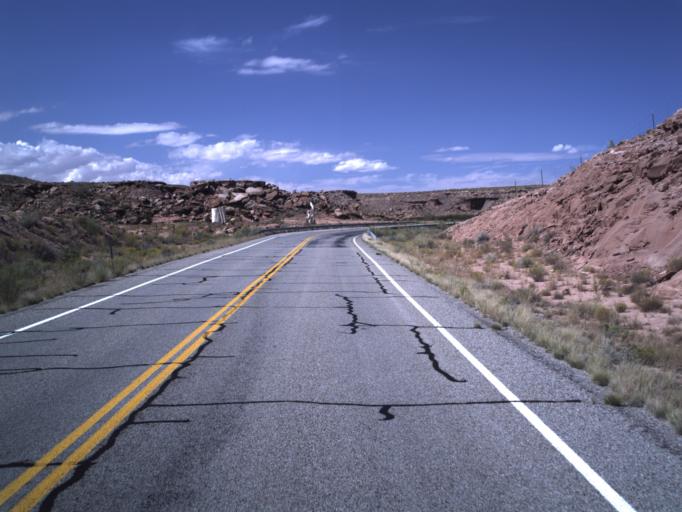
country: US
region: Utah
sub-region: San Juan County
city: Blanding
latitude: 37.2900
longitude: -109.4040
